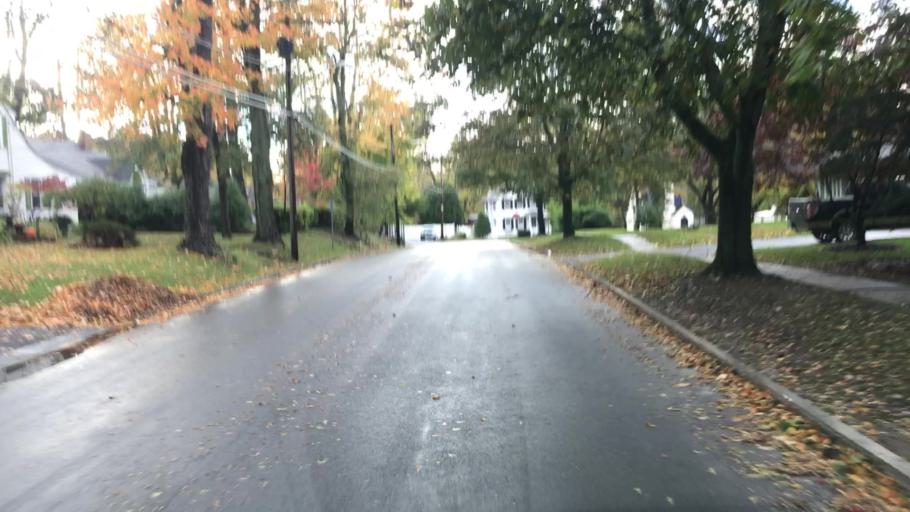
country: US
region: New York
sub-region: Onondaga County
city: Skaneateles
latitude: 42.9482
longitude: -76.4188
